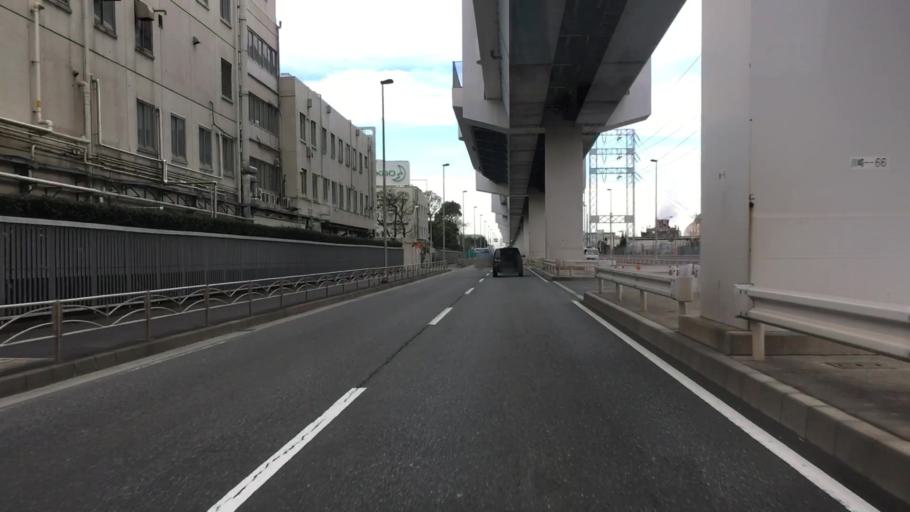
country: JP
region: Kanagawa
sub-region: Kawasaki-shi
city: Kawasaki
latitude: 35.5329
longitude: 139.7670
